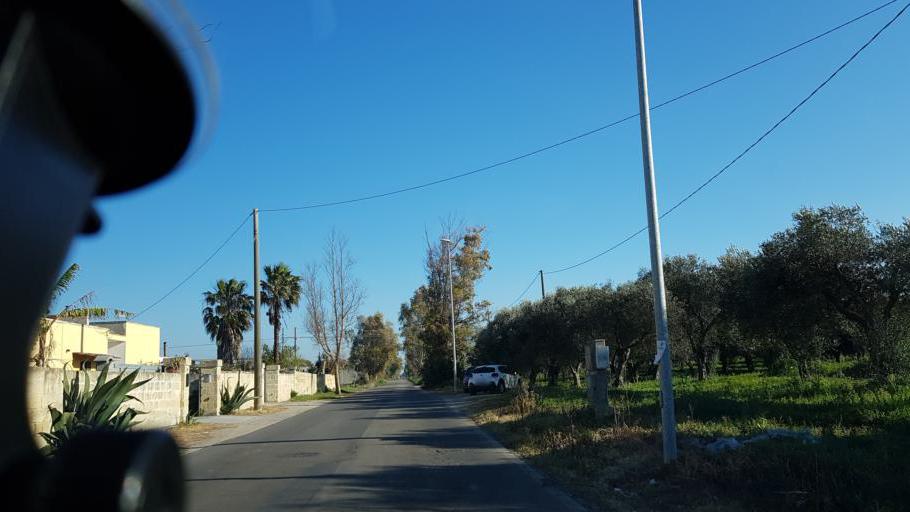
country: IT
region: Apulia
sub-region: Provincia di Lecce
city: Merine
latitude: 40.4247
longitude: 18.2454
